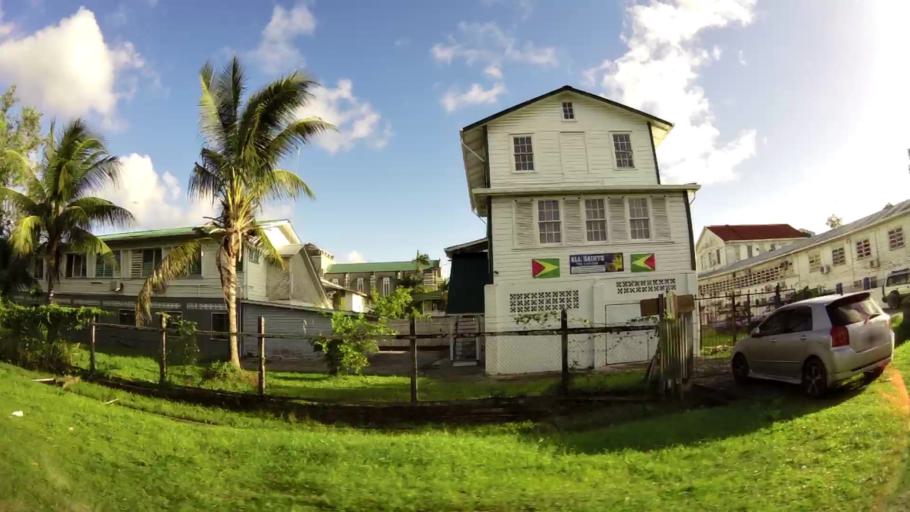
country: GY
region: Demerara-Mahaica
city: Georgetown
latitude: 6.8087
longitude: -58.1621
